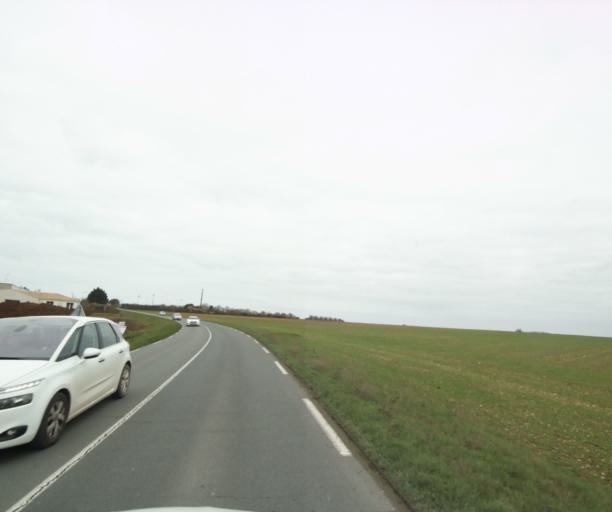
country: FR
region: Poitou-Charentes
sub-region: Departement de la Charente-Maritime
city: Lagord
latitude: 46.1926
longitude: -1.1482
